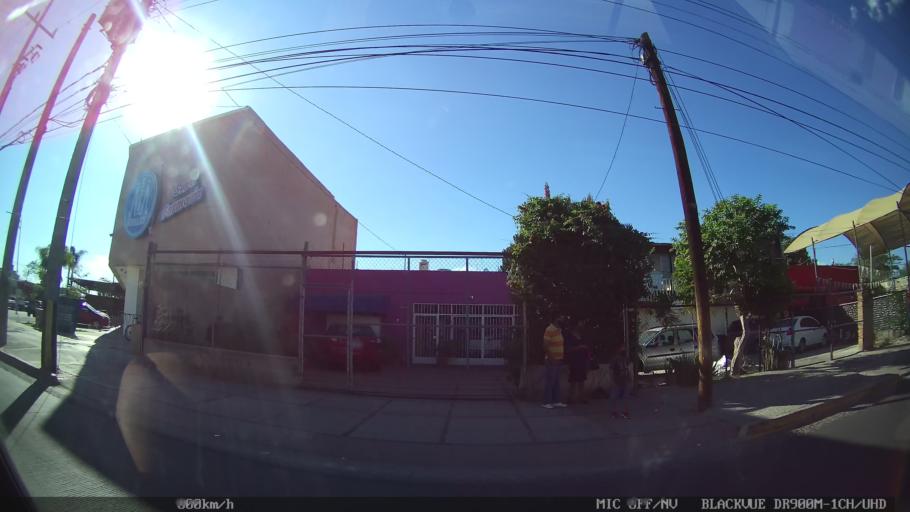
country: MX
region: Jalisco
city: Tlaquepaque
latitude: 20.7098
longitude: -103.3103
